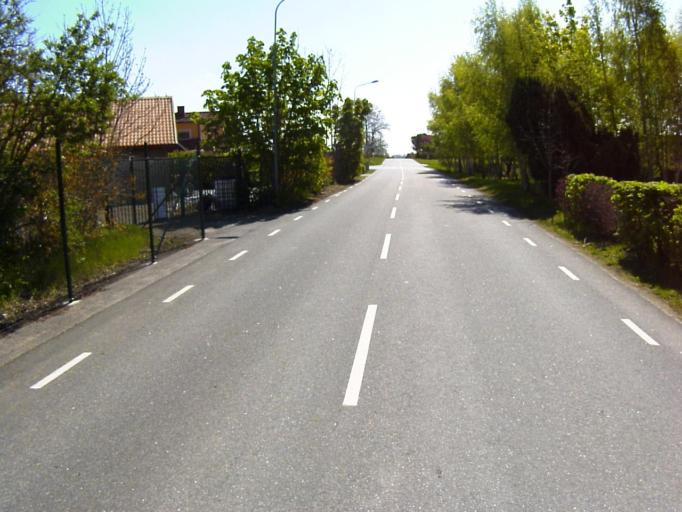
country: SE
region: Skane
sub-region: Kristianstads Kommun
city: Fjalkinge
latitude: 56.0100
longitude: 14.2446
